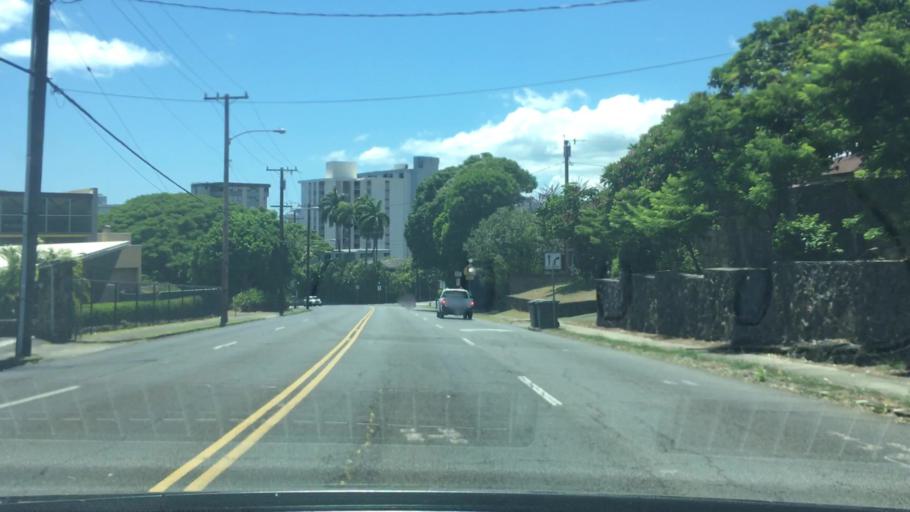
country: US
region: Hawaii
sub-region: Honolulu County
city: Honolulu
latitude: 21.3053
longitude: -157.8290
